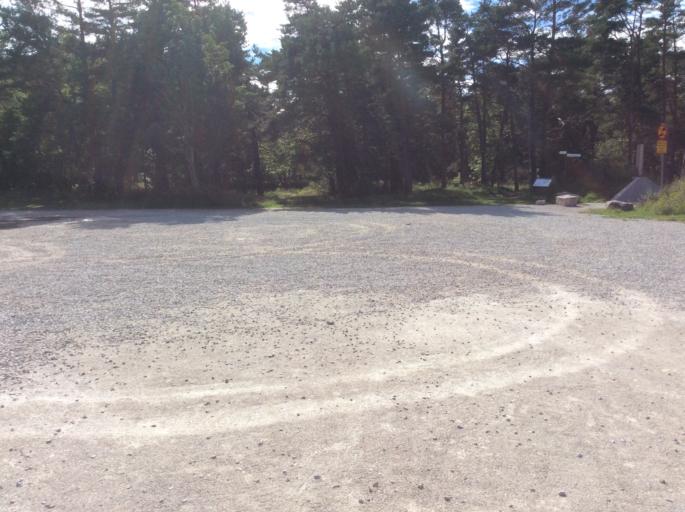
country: SE
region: Gotland
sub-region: Gotland
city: Vibble
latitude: 57.6180
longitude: 18.2686
